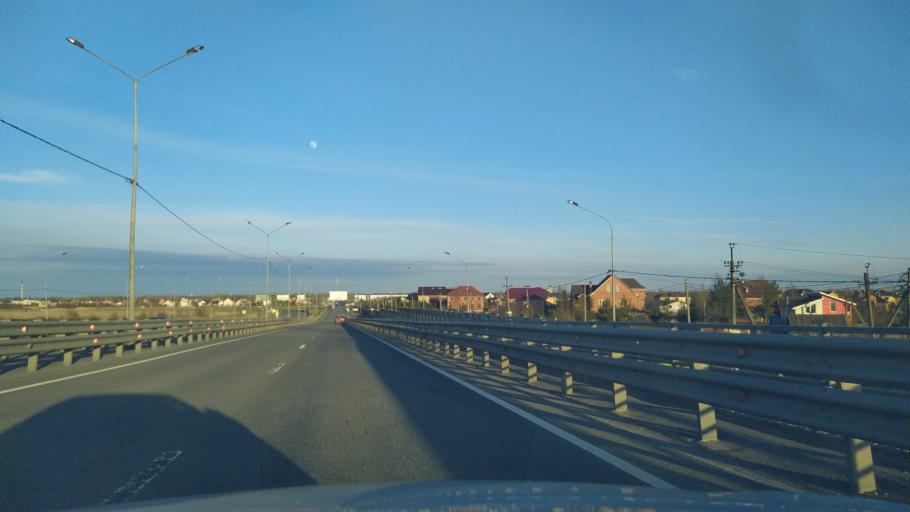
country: RU
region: St.-Petersburg
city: Aleksandrovskaya
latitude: 59.7433
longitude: 30.3131
